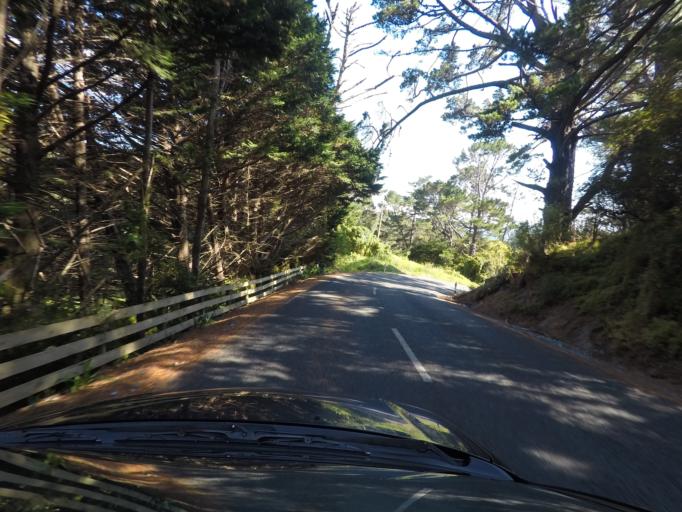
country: NZ
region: Auckland
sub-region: Auckland
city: Warkworth
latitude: -36.2807
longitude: 174.7912
